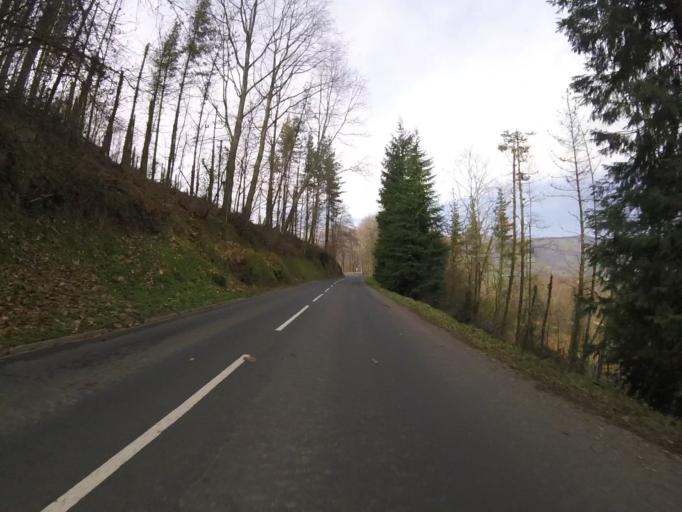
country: ES
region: Basque Country
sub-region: Provincia de Guipuzcoa
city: Beizama
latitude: 43.1643
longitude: -2.2142
